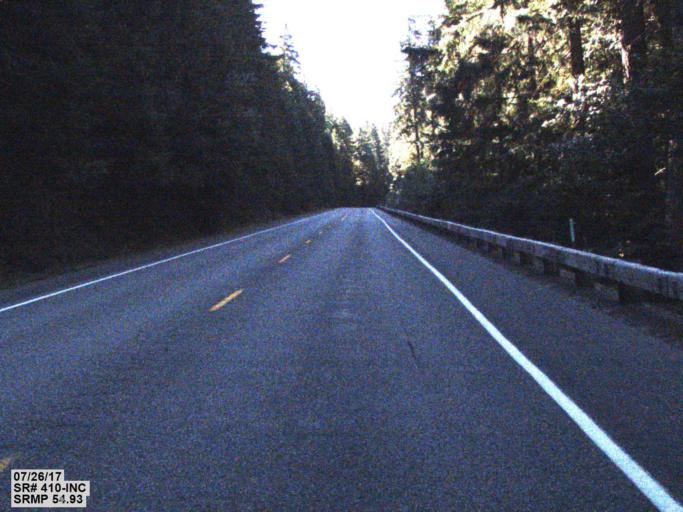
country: US
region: Washington
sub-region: King County
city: Enumclaw
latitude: 47.0159
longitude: -121.5296
